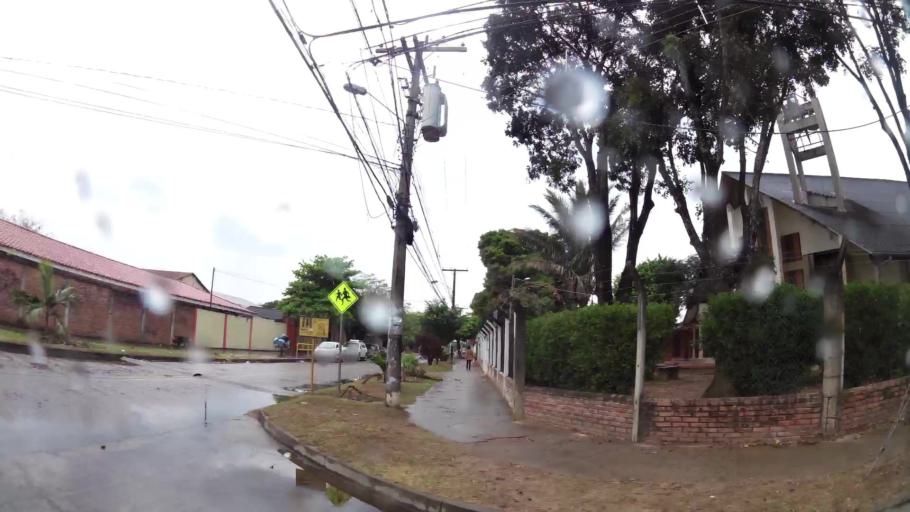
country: BO
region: Santa Cruz
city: Santa Cruz de la Sierra
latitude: -17.7986
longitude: -63.1565
